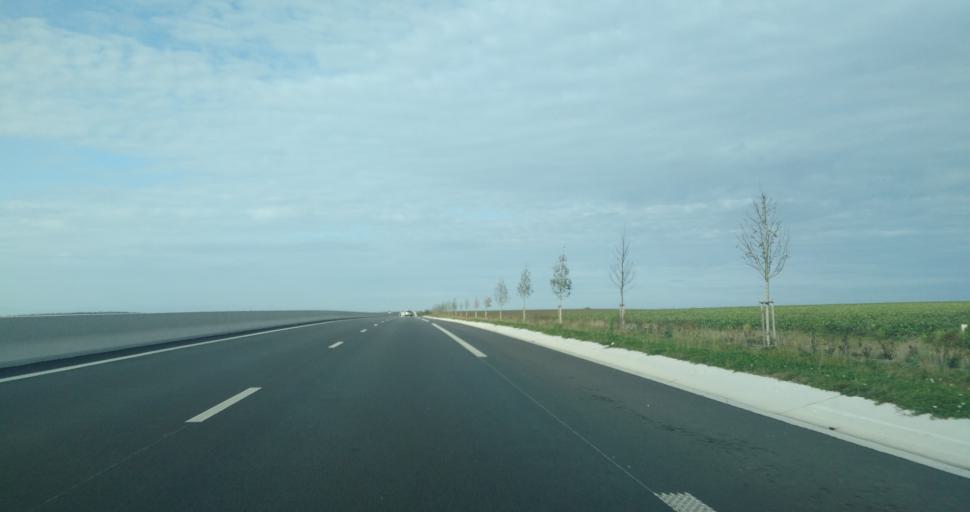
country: FR
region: Nord-Pas-de-Calais
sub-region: Departement du Pas-de-Calais
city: Duisans
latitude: 50.3196
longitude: 2.6730
